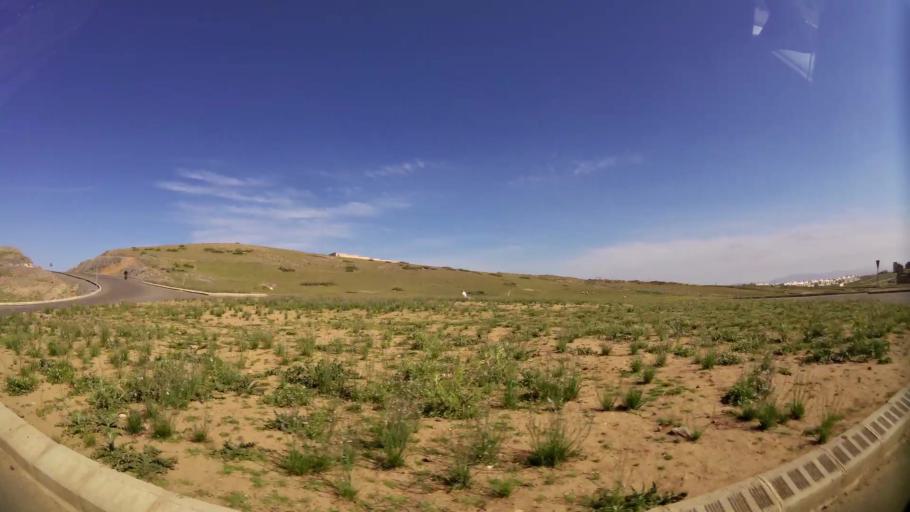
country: MA
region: Oriental
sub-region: Oujda-Angad
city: Oujda
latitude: 34.6474
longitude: -1.9486
